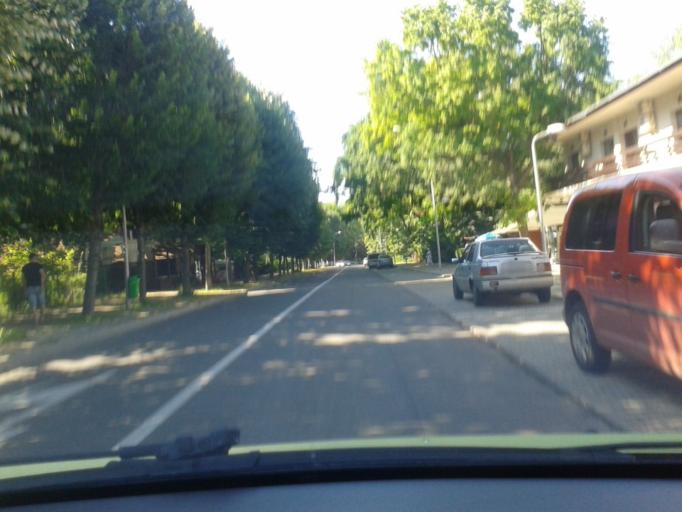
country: RO
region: Constanta
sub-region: Comuna Douazeci si Trei August
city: Douazeci si Trei August
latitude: 43.8770
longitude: 28.6030
